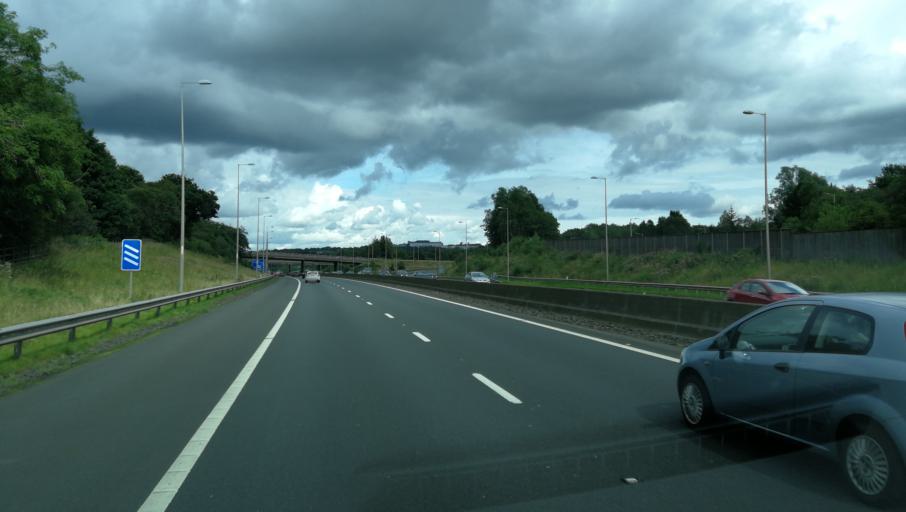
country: GB
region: Scotland
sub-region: North Lanarkshire
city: Cumbernauld
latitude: 55.9386
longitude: -4.0242
